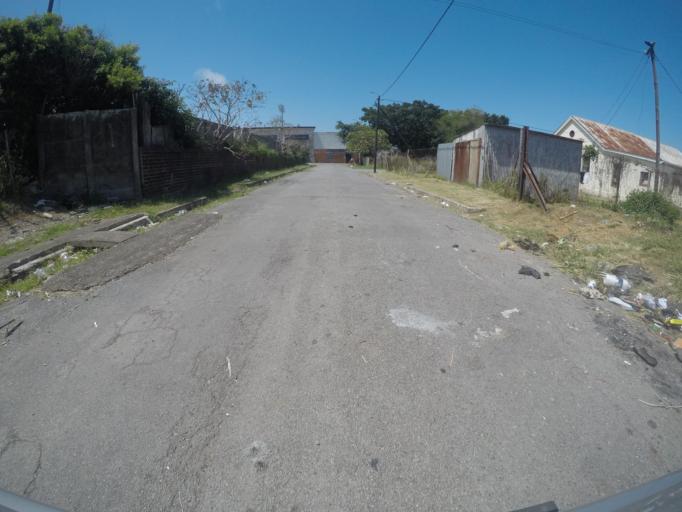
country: ZA
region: Eastern Cape
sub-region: Buffalo City Metropolitan Municipality
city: East London
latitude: -33.0097
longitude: 27.9038
